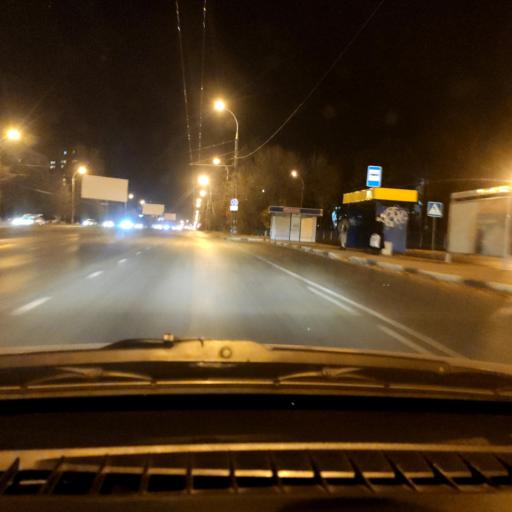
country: RU
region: Samara
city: Tol'yatti
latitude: 53.5205
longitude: 49.3175
